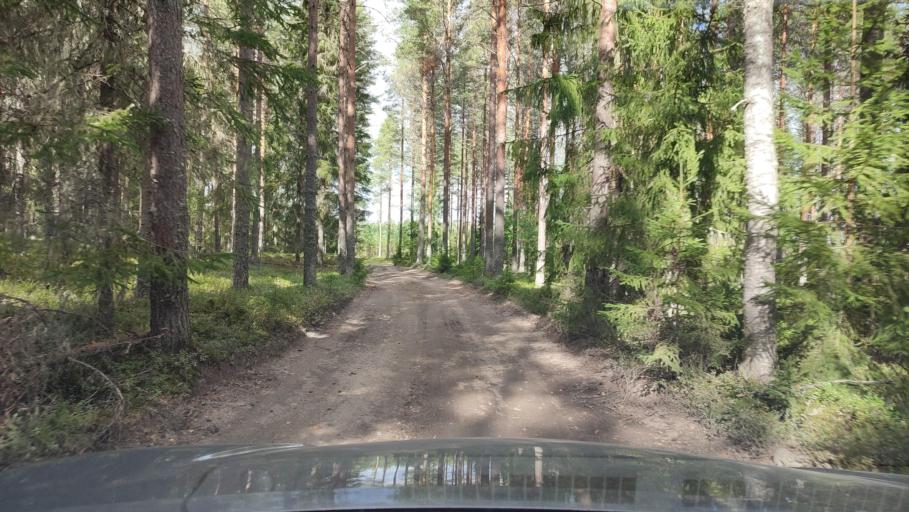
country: FI
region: Southern Ostrobothnia
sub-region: Suupohja
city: Karijoki
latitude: 62.2177
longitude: 21.6259
